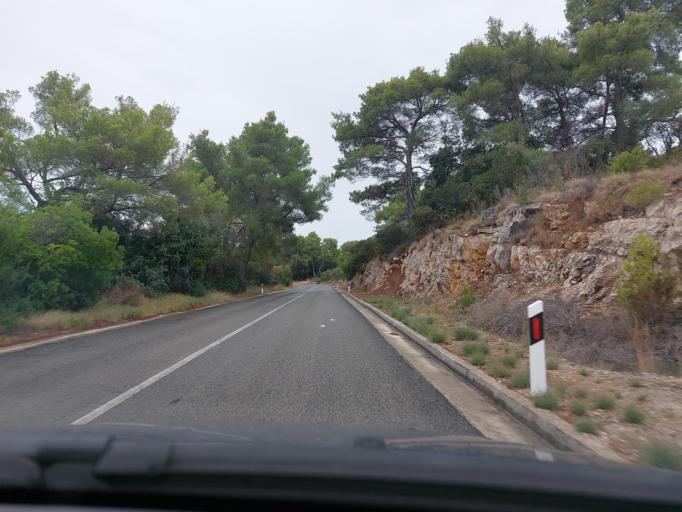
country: HR
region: Dubrovacko-Neretvanska
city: Smokvica
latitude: 42.7677
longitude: 16.8719
